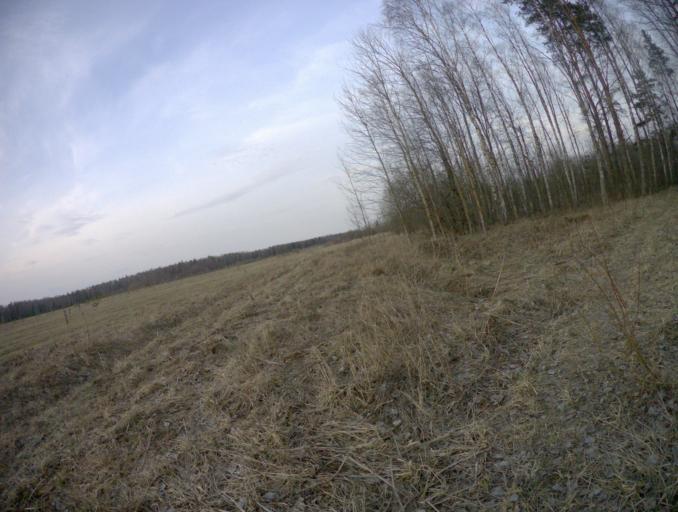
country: RU
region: Vladimir
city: Kommunar
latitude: 56.0768
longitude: 40.5353
